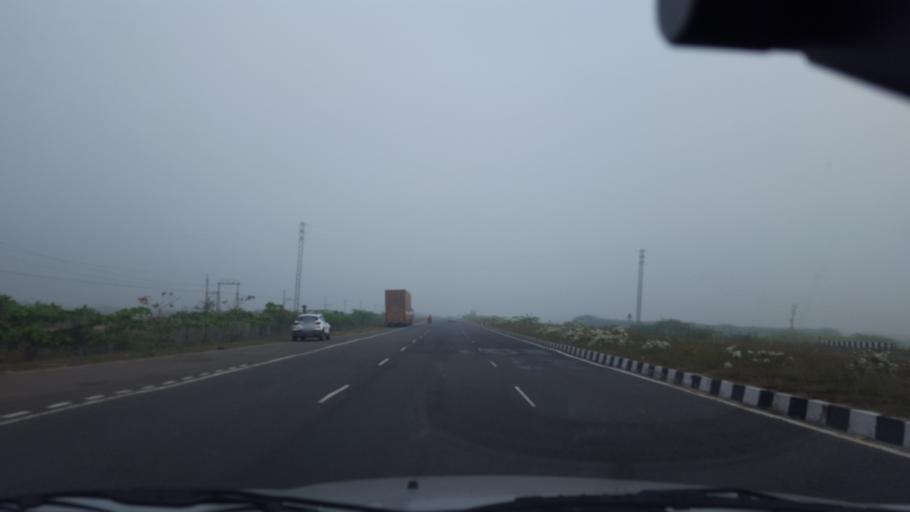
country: IN
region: Andhra Pradesh
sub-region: Prakasam
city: Ongole
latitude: 15.4791
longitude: 80.0602
